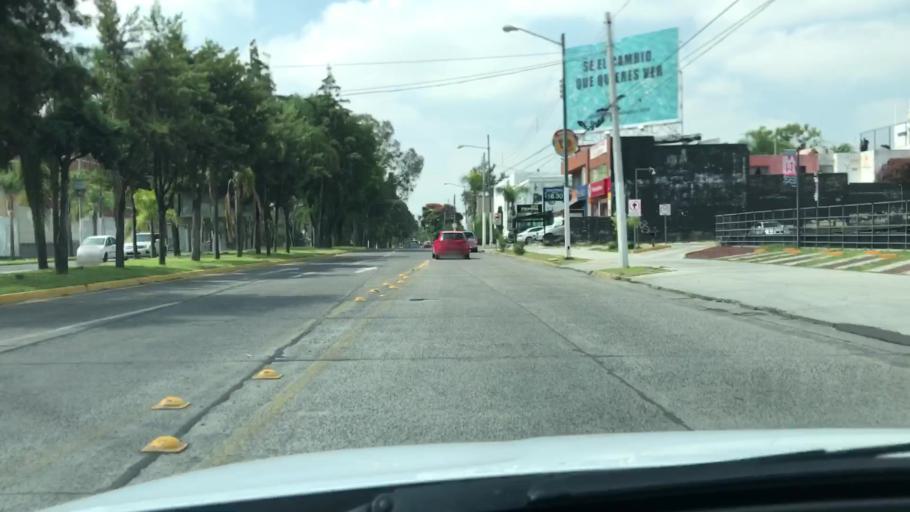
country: MX
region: Jalisco
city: Guadalajara
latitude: 20.6762
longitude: -103.4223
